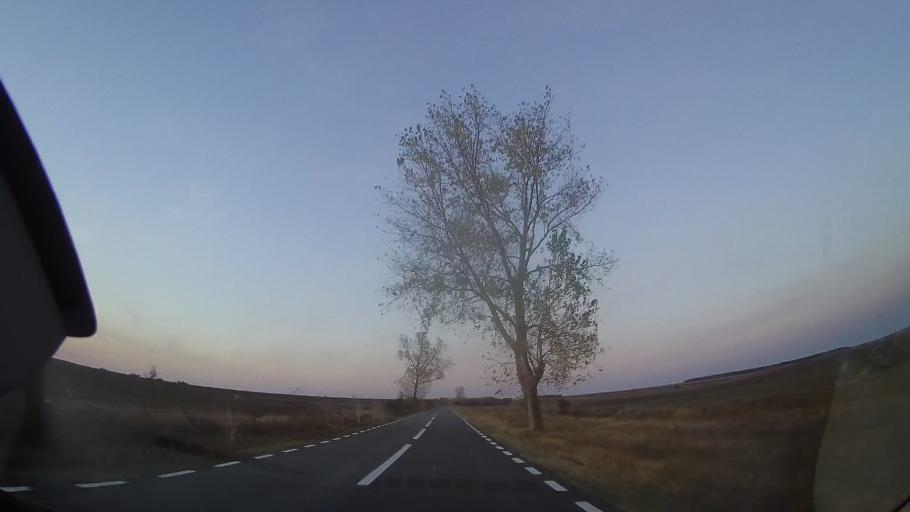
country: RO
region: Constanta
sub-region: Comuna Cobadin
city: Cobadin
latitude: 44.0281
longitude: 28.2626
